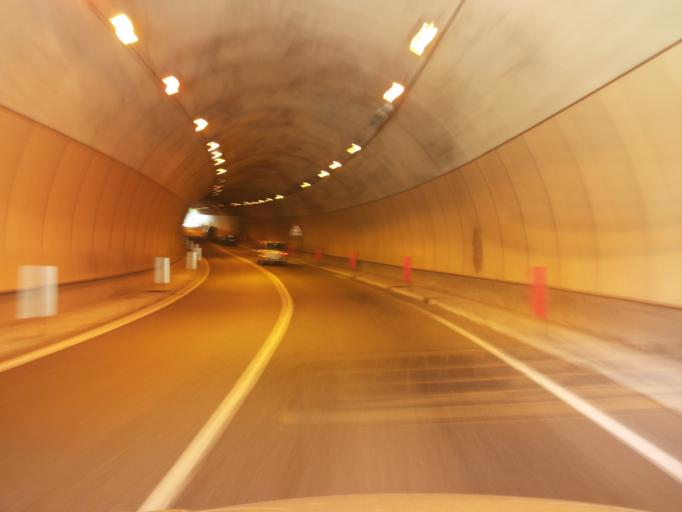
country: IT
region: Aosta Valley
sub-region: Valle d'Aosta
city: Perloz
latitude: 45.6111
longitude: 7.8158
